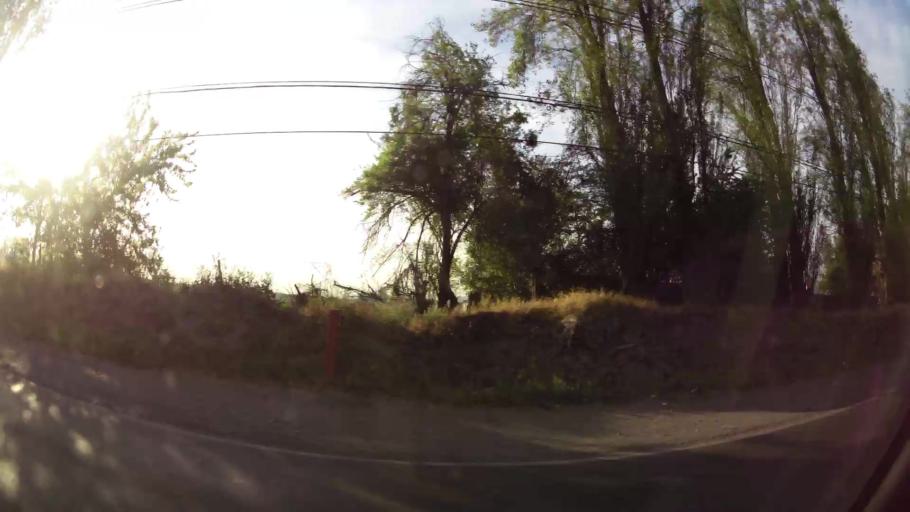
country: CL
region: Santiago Metropolitan
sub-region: Provincia de Maipo
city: San Bernardo
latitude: -33.5555
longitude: -70.7537
